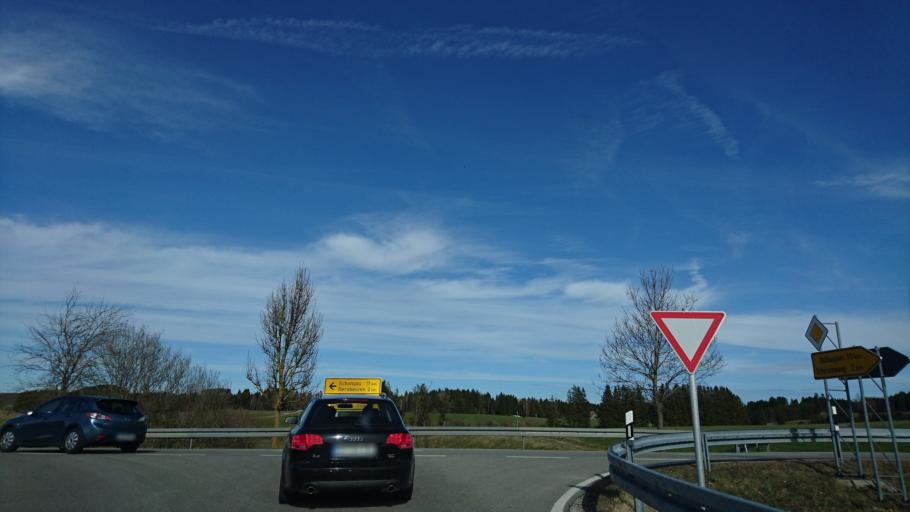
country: DE
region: Bavaria
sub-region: Upper Bavaria
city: Bernbeuren
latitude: 47.7241
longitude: 10.7862
